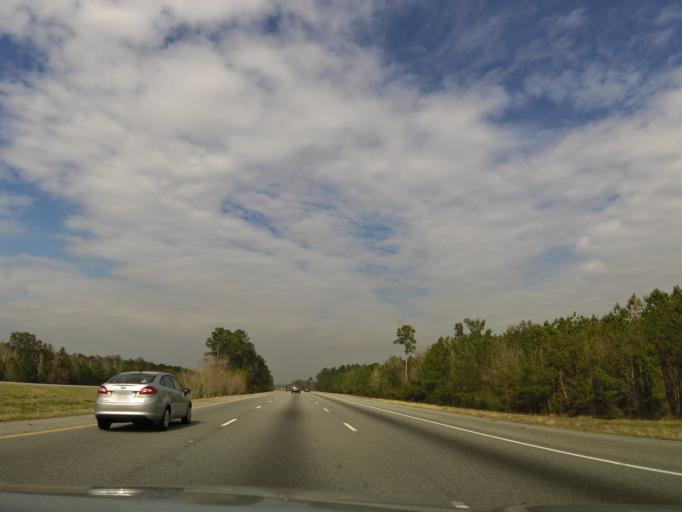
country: US
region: Georgia
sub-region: Liberty County
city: Midway
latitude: 31.7449
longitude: -81.3850
